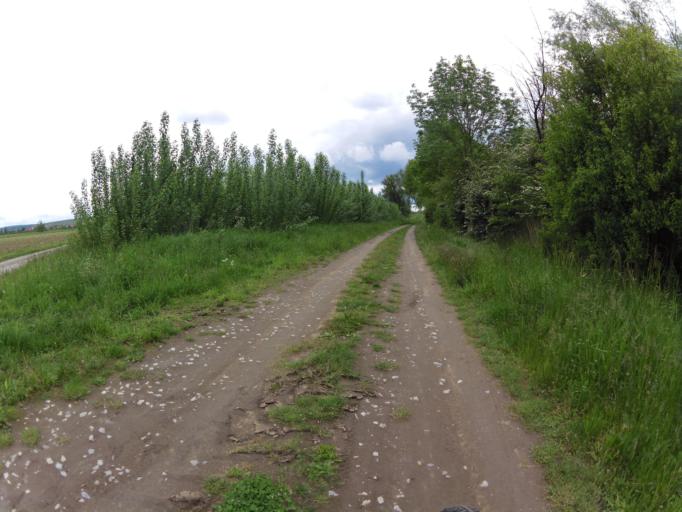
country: DE
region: Bavaria
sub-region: Regierungsbezirk Unterfranken
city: Sommerach
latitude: 49.8201
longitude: 10.2184
